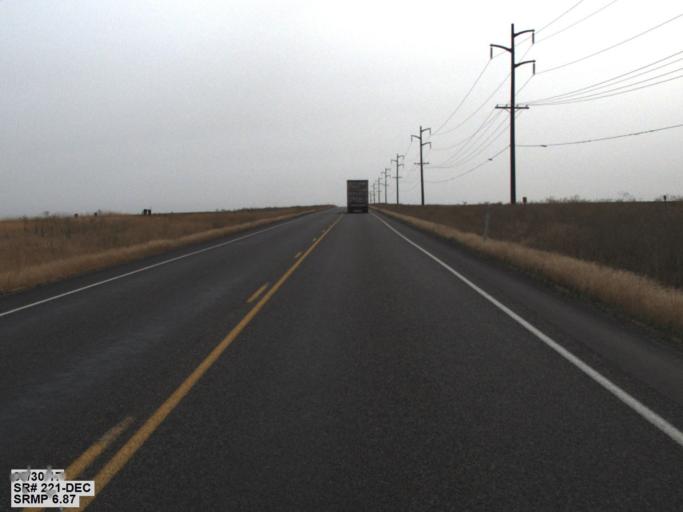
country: US
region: Oregon
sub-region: Morrow County
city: Irrigon
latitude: 46.0347
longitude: -119.6026
